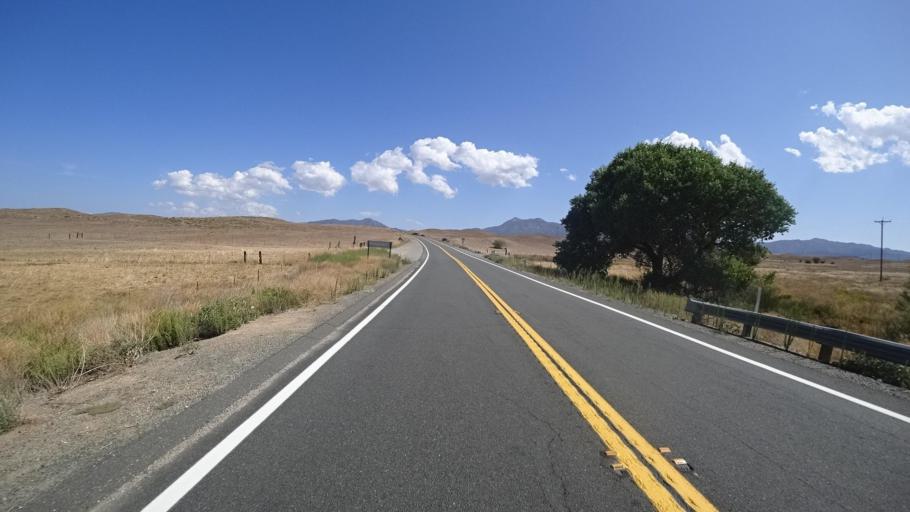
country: US
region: California
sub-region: San Diego County
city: Julian
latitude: 33.2518
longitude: -116.6707
